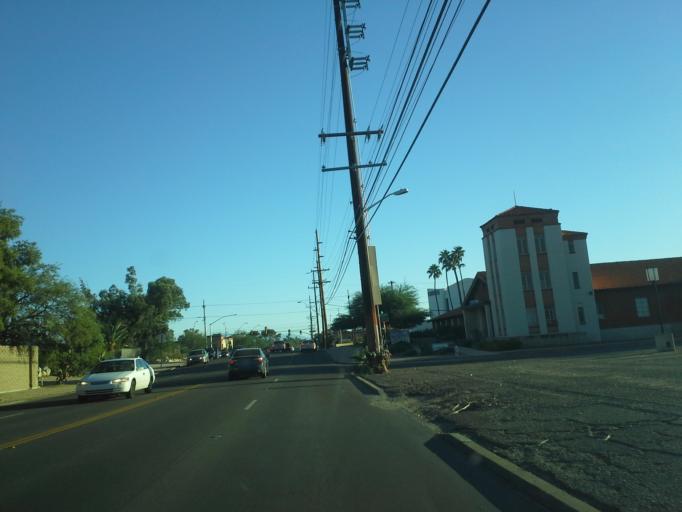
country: US
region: Arizona
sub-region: Pima County
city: Tucson
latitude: 32.2233
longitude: -110.9267
